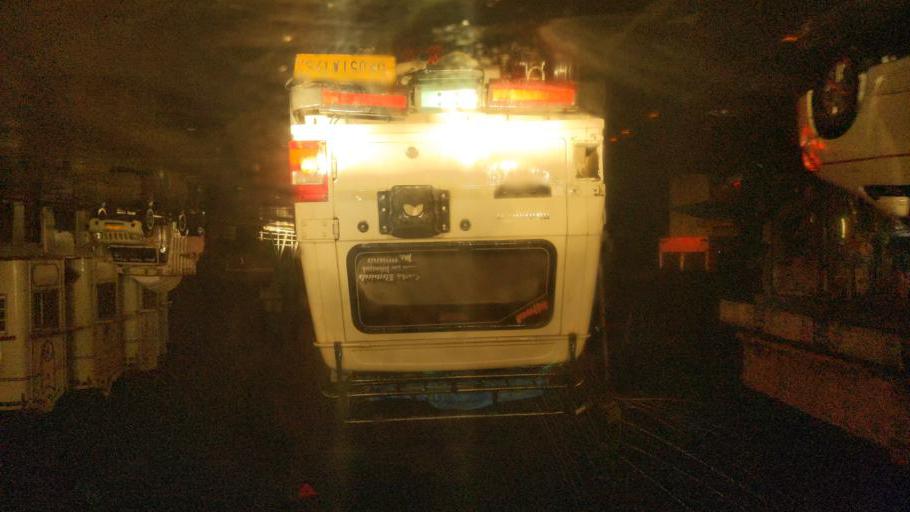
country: IN
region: Uttarakhand
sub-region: Naini Tal
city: Haldwani
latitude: 29.2712
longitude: 79.5441
